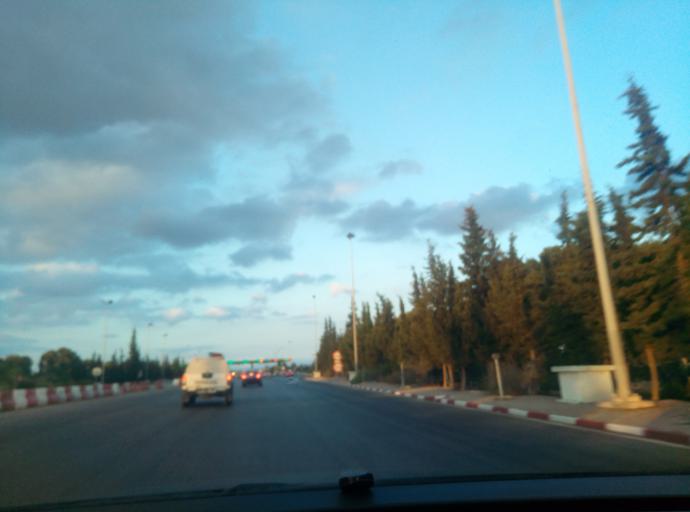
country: TN
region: Tunis
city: Oued Lill
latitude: 36.7117
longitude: 9.9721
